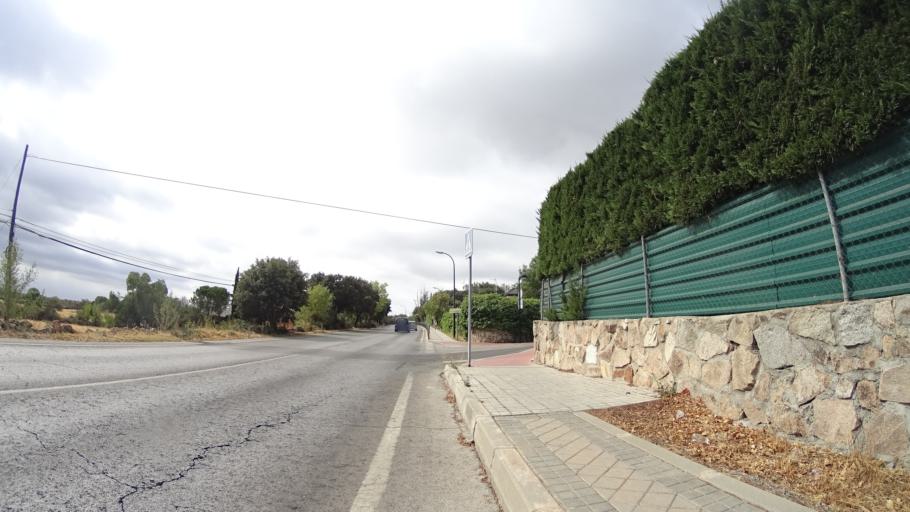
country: ES
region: Madrid
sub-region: Provincia de Madrid
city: Galapagar
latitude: 40.5883
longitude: -4.0118
